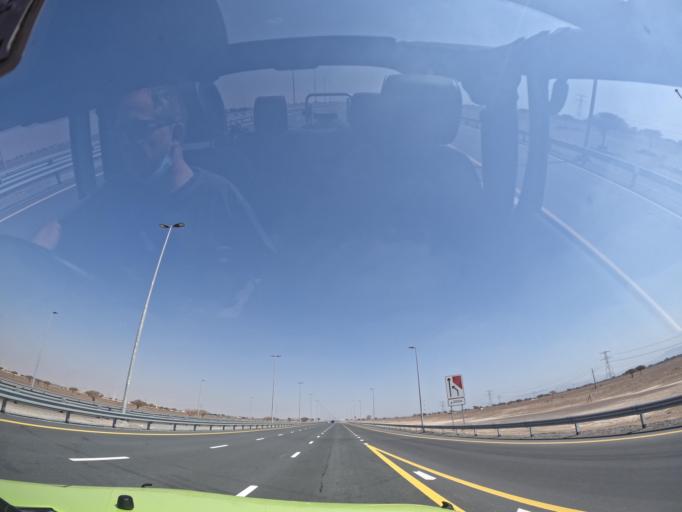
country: AE
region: Ash Shariqah
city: Adh Dhayd
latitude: 24.9579
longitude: 55.8395
